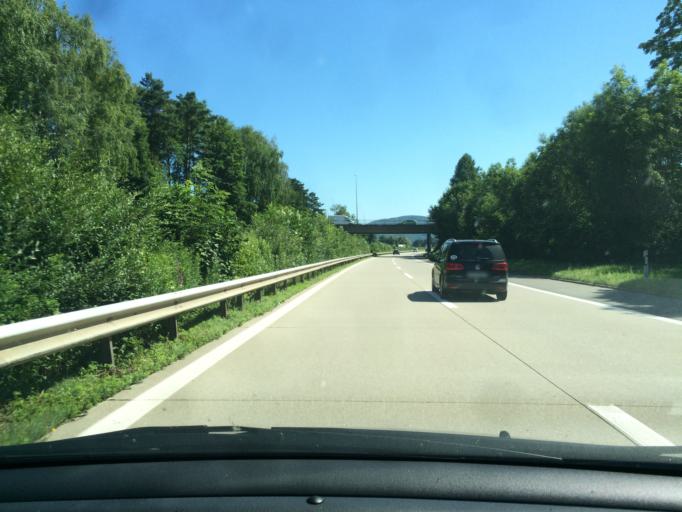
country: CH
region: Saint Gallen
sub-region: Wahlkreis Rheintal
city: Oberriet
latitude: 47.3069
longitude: 9.5673
